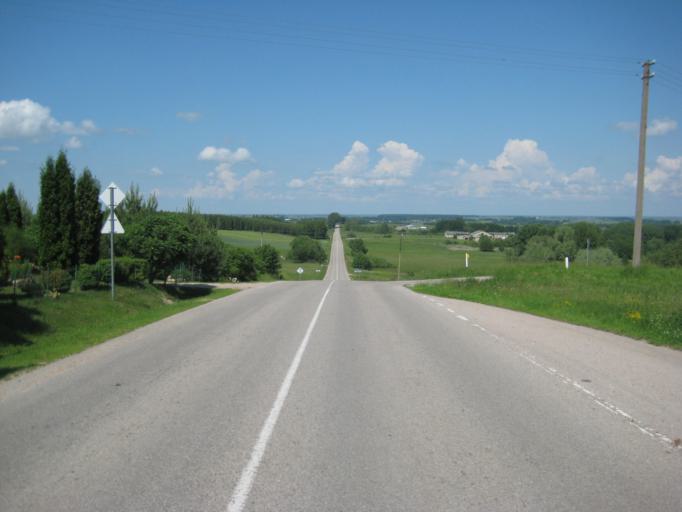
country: LT
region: Taurages apskritis
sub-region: Jurbarkas
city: Jurbarkas
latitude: 55.0427
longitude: 22.6440
